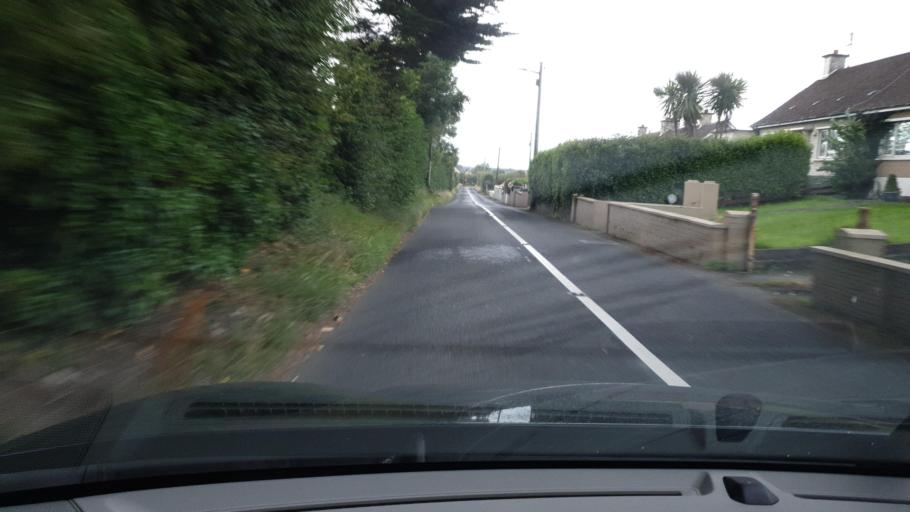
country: IE
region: Leinster
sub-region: South Dublin
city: Rathcoole
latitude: 53.2724
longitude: -6.4873
